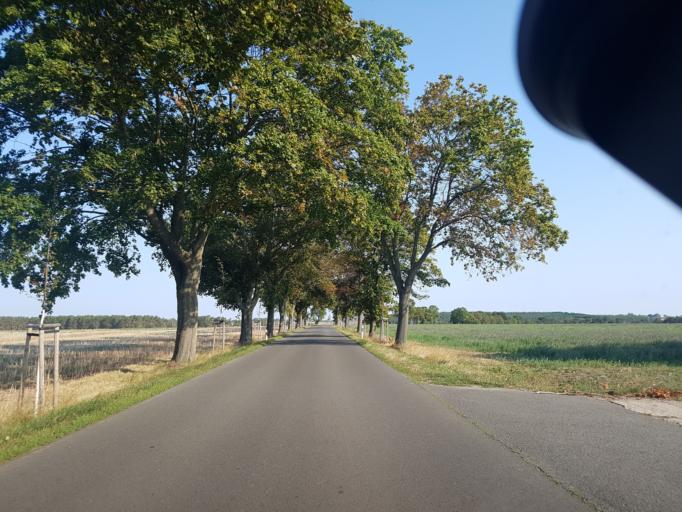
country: DE
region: Saxony-Anhalt
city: Kropstadt
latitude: 51.9957
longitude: 12.6805
